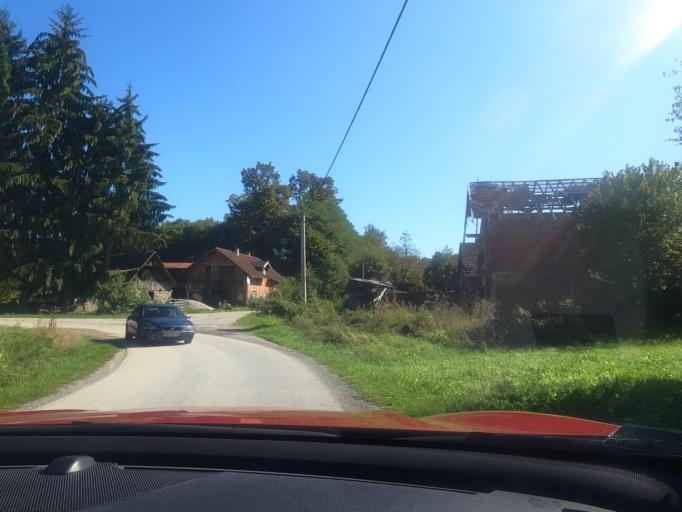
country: HR
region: Sisacko-Moslavacka
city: Petrinja
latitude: 45.4142
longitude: 16.2575
